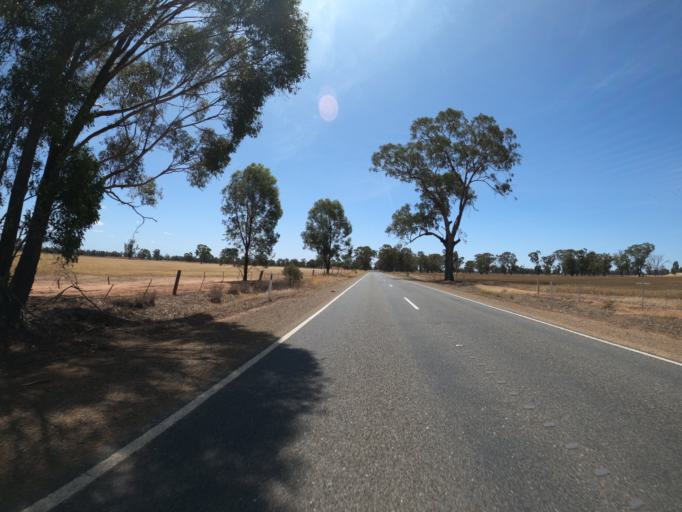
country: AU
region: Victoria
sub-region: Moira
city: Yarrawonga
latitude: -36.1865
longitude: 145.9672
